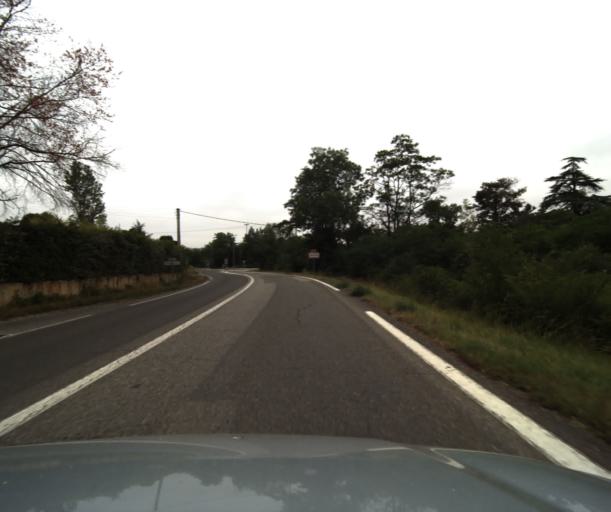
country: FR
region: Midi-Pyrenees
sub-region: Departement du Gers
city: Auch
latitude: 43.6535
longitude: 0.6130
